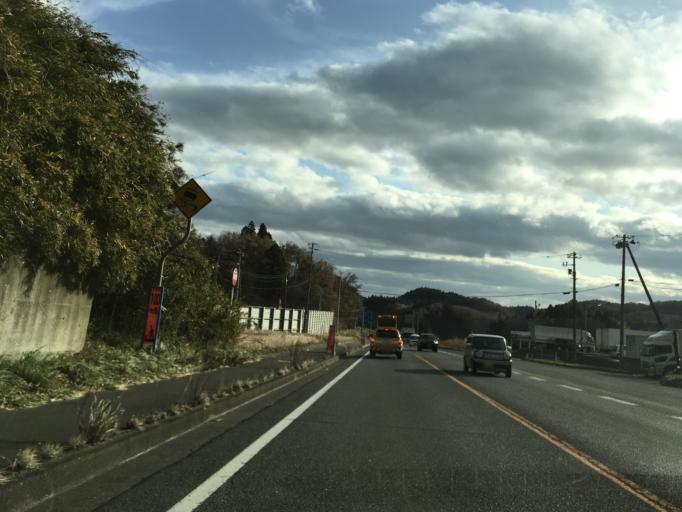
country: JP
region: Iwate
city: Ichinoseki
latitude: 38.8935
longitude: 141.1158
